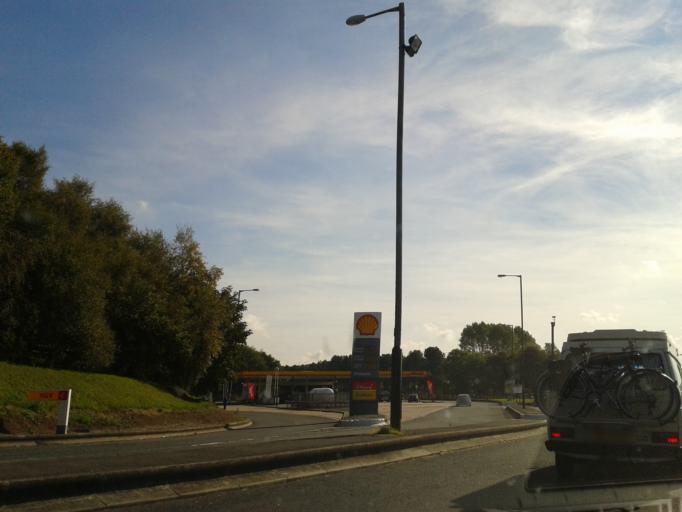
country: GB
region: England
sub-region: Staffordshire
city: Newcastle under Lyme
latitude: 52.9943
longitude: -2.2895
